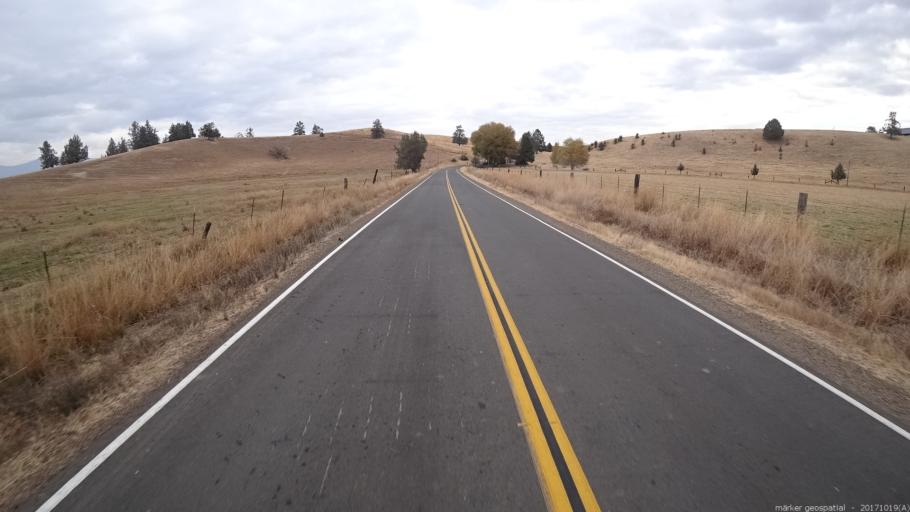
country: US
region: California
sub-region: Shasta County
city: Burney
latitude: 41.0390
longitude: -121.3529
